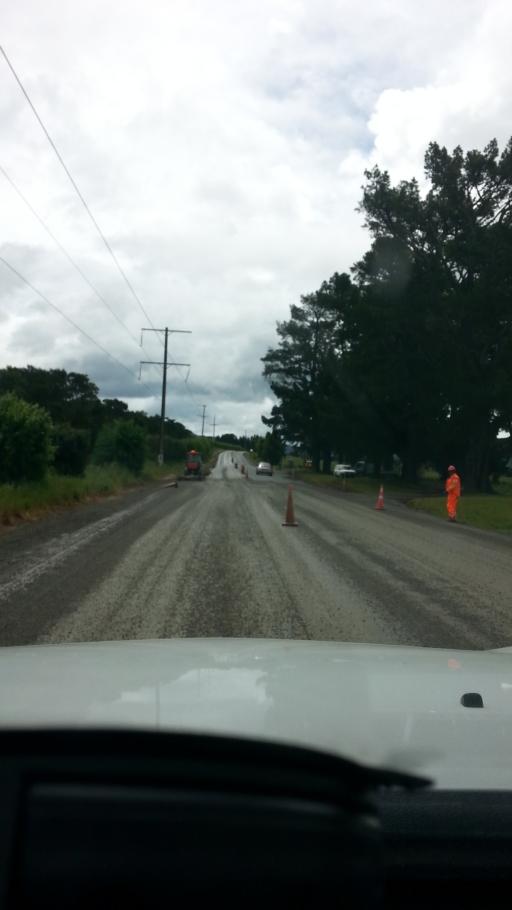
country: NZ
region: Wellington
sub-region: Masterton District
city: Masterton
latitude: -40.8274
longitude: 175.6259
